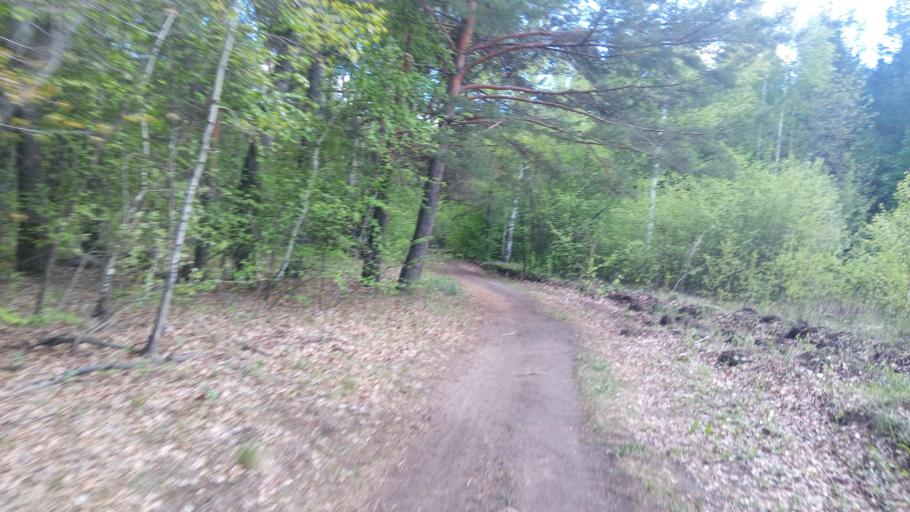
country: RU
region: Chelyabinsk
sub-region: Gorod Chelyabinsk
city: Chelyabinsk
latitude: 55.1639
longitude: 61.3155
